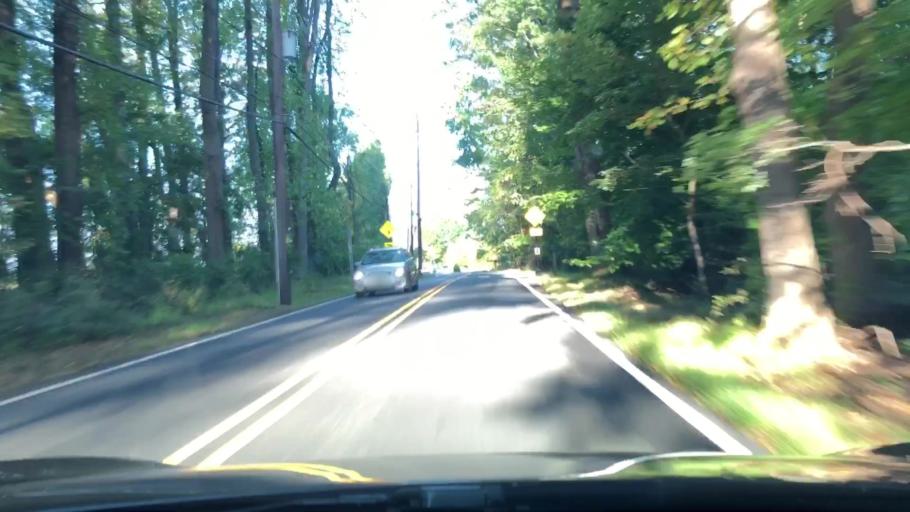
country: US
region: New Jersey
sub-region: Mercer County
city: Lawrenceville
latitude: 40.3096
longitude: -74.7420
